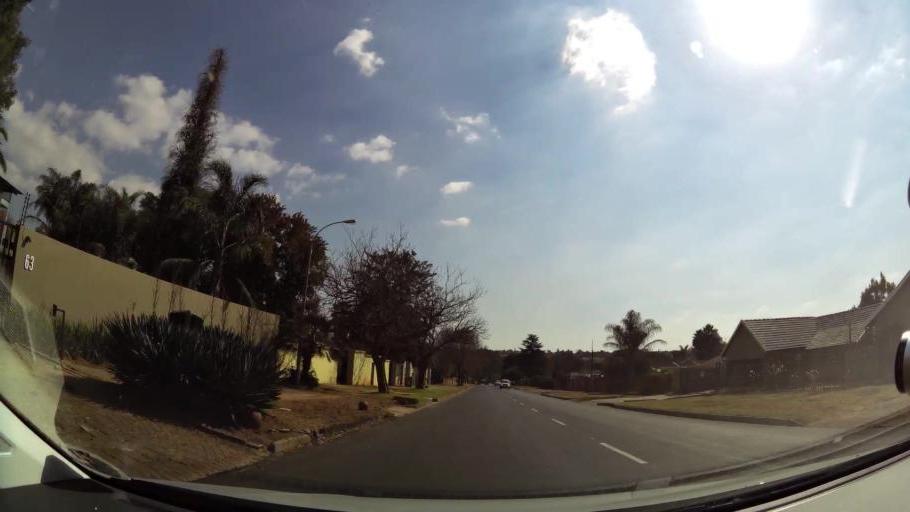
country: ZA
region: Gauteng
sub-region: City of Johannesburg Metropolitan Municipality
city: Modderfontein
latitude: -26.0735
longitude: 28.2359
